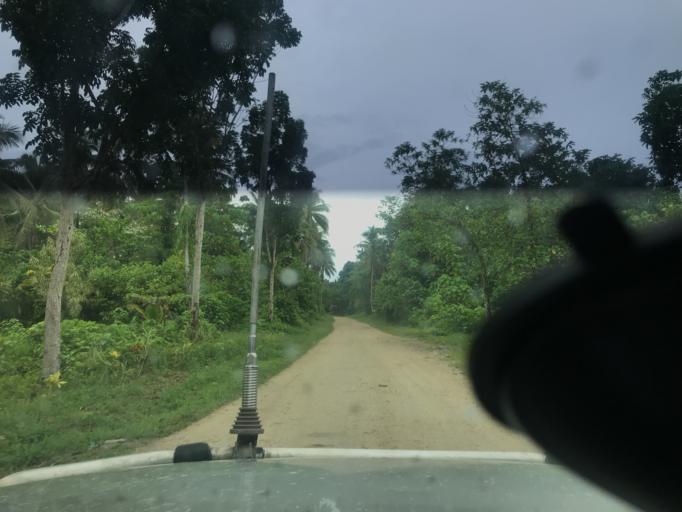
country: SB
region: Choiseul
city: Taro'a
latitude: -9.1844
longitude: 160.9366
